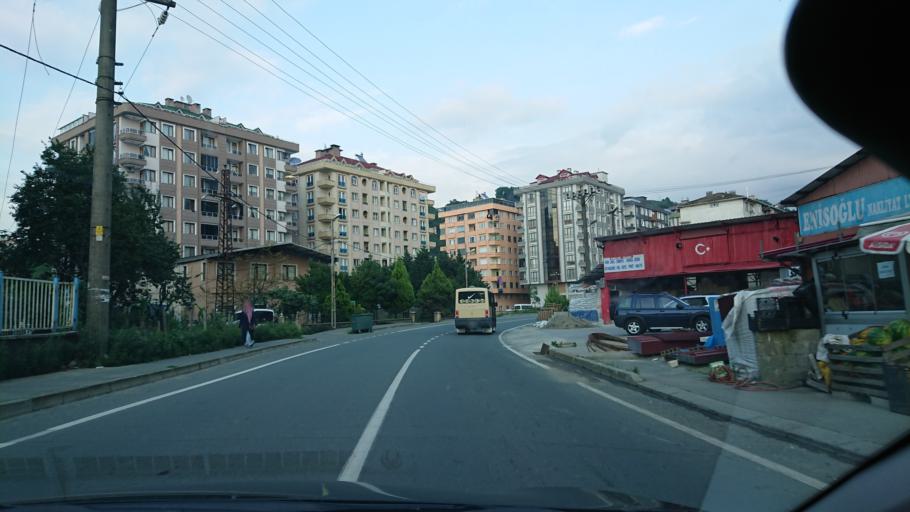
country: TR
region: Rize
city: Cayeli
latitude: 41.0822
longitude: 40.7108
